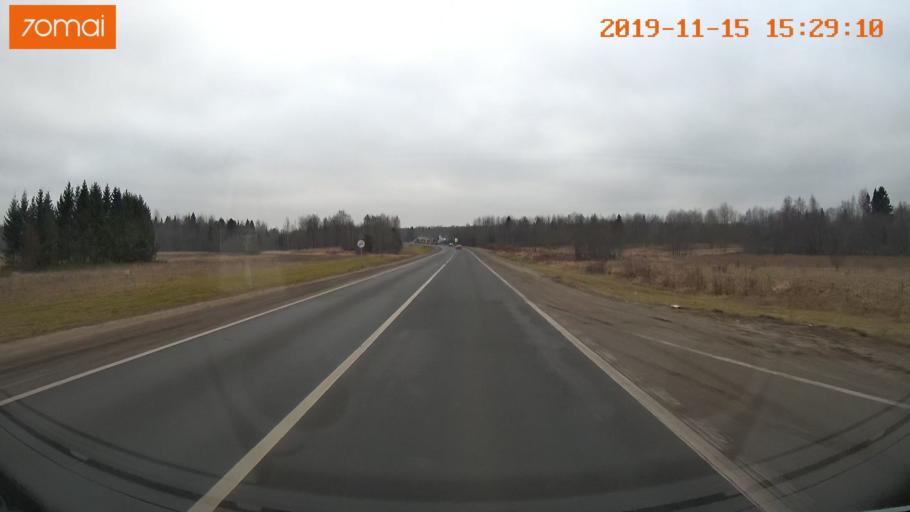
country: RU
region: Jaroslavl
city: Danilov
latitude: 58.1237
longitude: 40.1237
